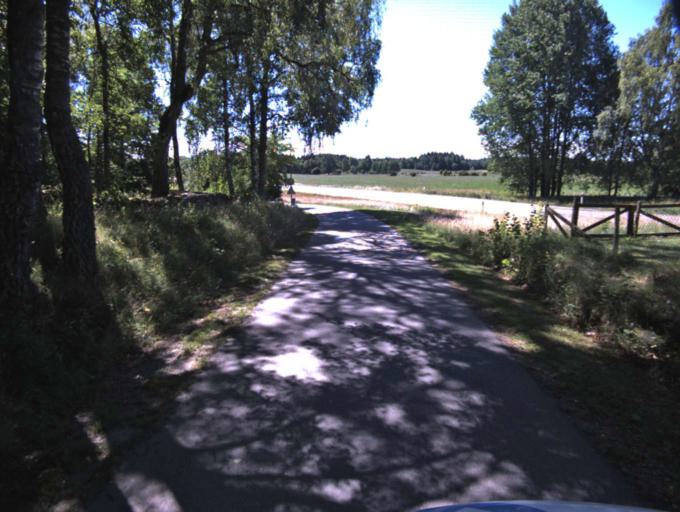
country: SE
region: Vaestra Goetaland
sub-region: Ulricehamns Kommun
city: Ulricehamn
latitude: 57.6620
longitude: 13.4305
